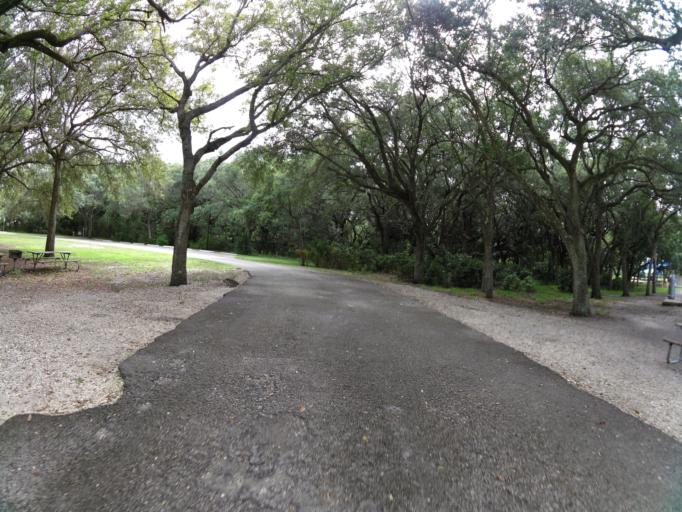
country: US
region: Florida
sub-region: Broward County
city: Cooper City
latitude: 26.0700
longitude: -80.2740
